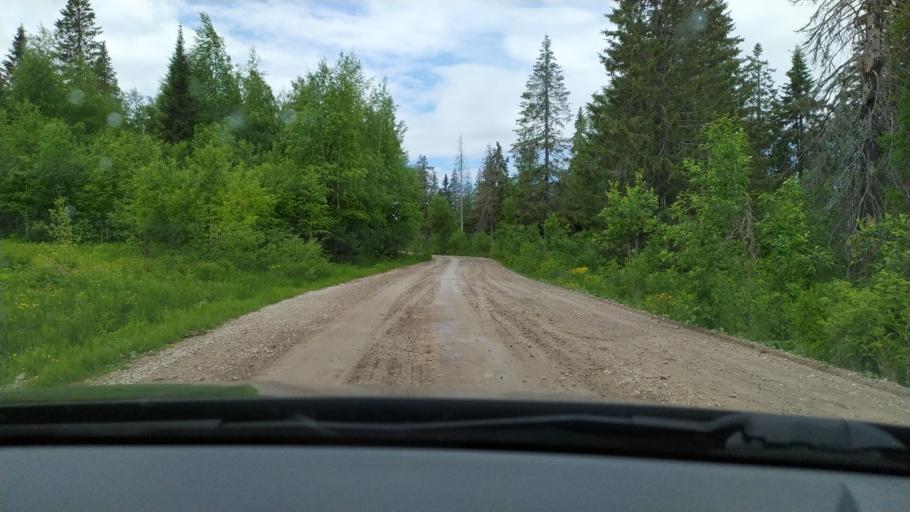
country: RU
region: Perm
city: Gremyachinsk
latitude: 58.5106
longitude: 57.8174
